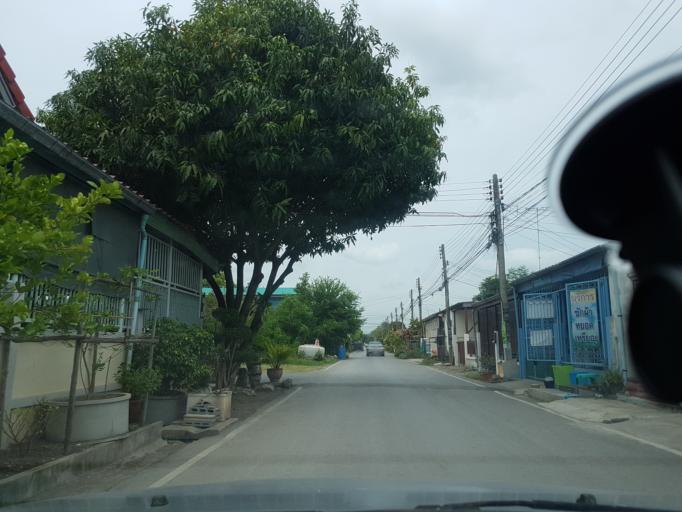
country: TH
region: Lop Buri
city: Lop Buri
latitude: 14.7714
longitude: 100.6916
